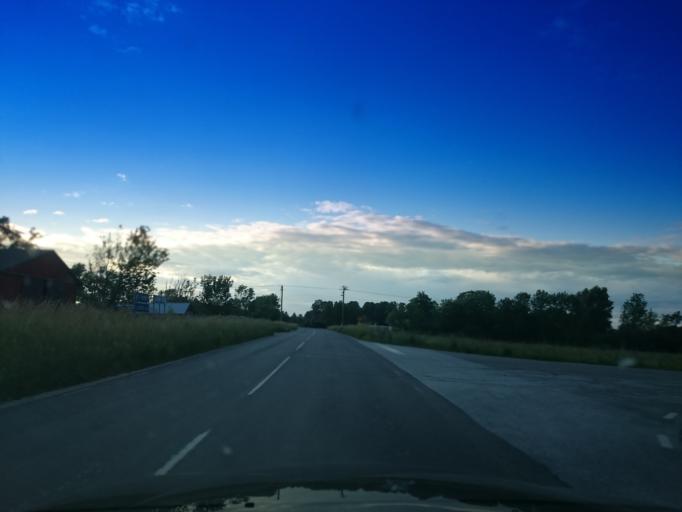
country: SE
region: Gotland
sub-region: Gotland
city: Hemse
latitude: 57.3215
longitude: 18.3848
